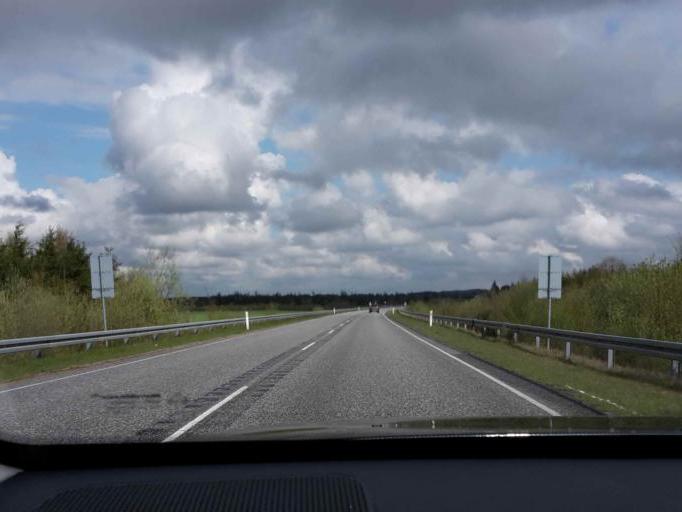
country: DK
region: South Denmark
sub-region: Billund Kommune
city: Billund
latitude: 55.7169
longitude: 9.2166
